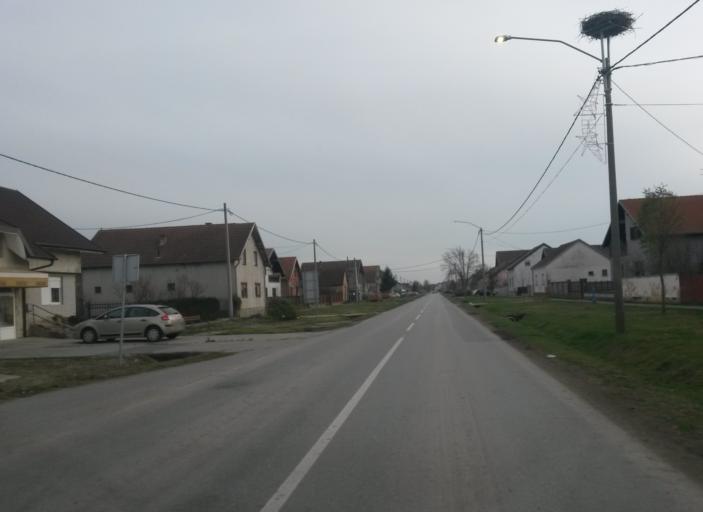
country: HR
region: Osjecko-Baranjska
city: Antunovac
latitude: 45.4856
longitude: 18.6369
